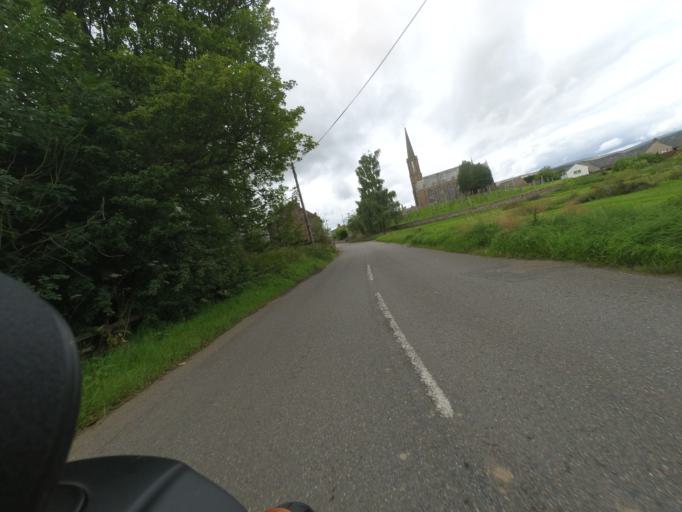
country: GB
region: Scotland
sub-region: Aberdeenshire
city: Laurencekirk
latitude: 56.8512
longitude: -2.5725
